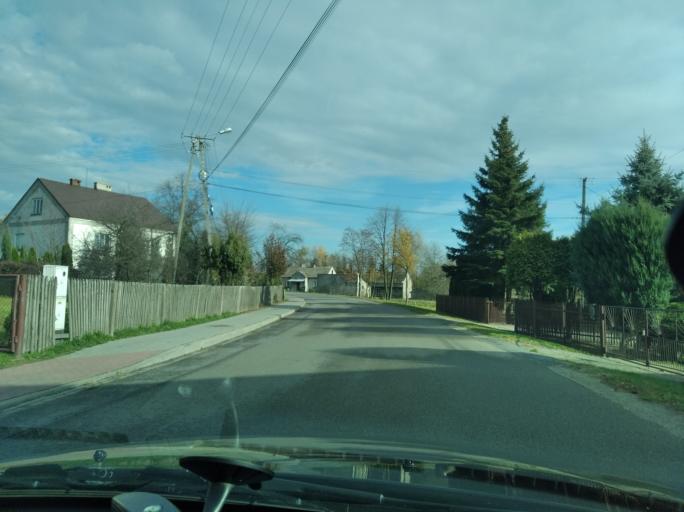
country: PL
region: Subcarpathian Voivodeship
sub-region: Powiat ropczycko-sedziszowski
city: Ostrow
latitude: 50.0997
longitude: 21.5968
